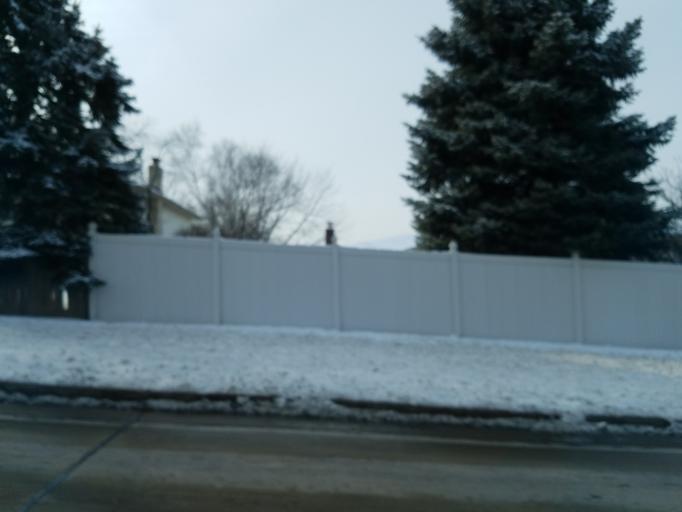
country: US
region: Illinois
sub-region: Cook County
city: Orland Hills
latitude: 41.6135
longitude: -87.8142
